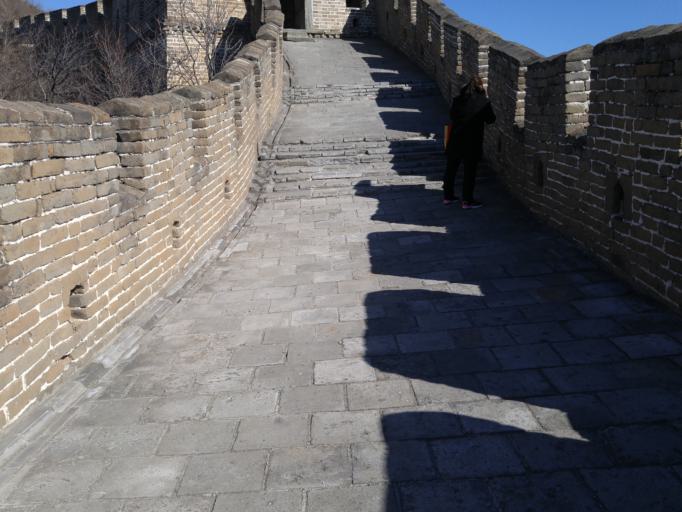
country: CN
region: Beijing
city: Bohai
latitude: 40.4382
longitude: 116.5612
